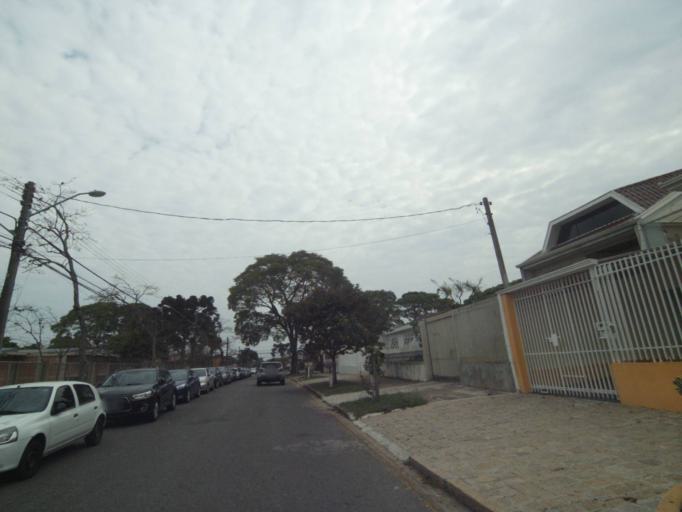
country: BR
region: Parana
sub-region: Curitiba
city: Curitiba
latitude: -25.4631
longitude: -49.3064
